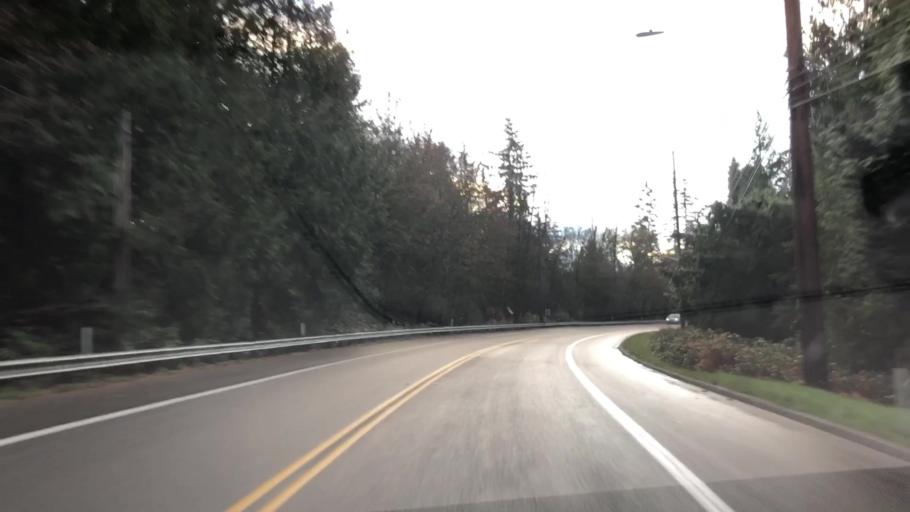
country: US
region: Washington
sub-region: King County
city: City of Sammamish
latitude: 47.6343
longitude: -122.0363
